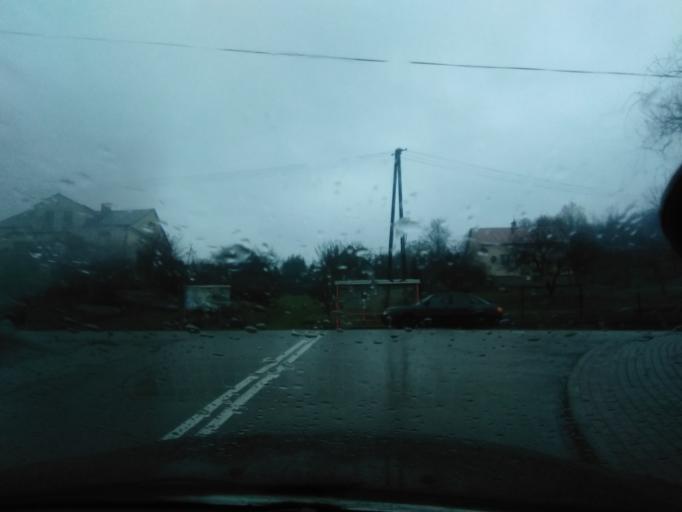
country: PL
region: Subcarpathian Voivodeship
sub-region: Powiat krosnienski
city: Kroscienko Wyzne
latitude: 49.6790
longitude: 21.8339
